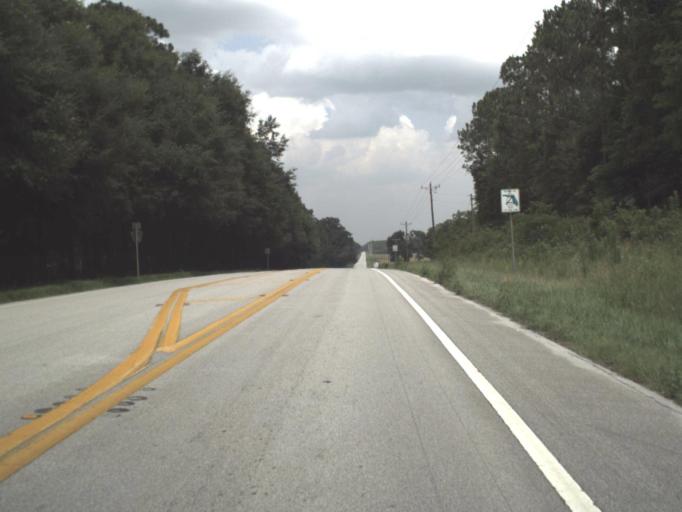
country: US
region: Florida
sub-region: Madison County
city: Madison
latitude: 30.4722
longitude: -83.2988
